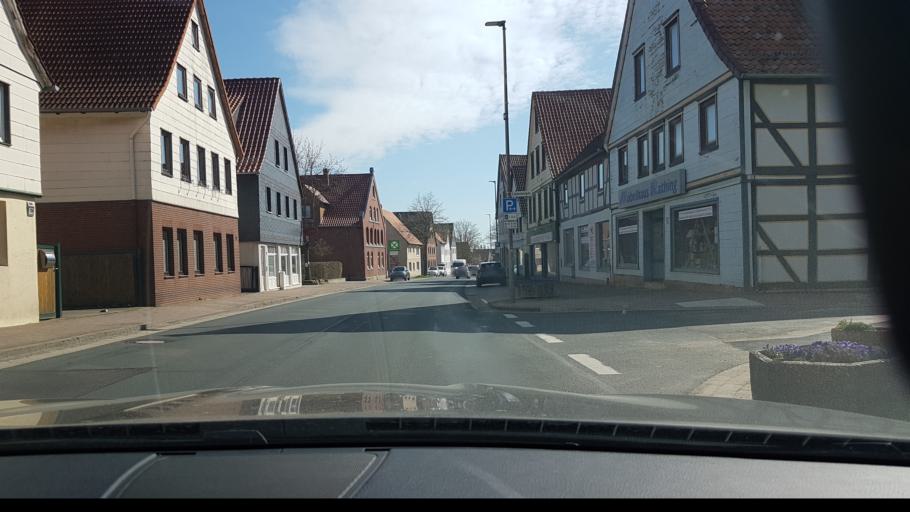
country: DE
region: Lower Saxony
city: Elze
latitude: 52.1833
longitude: 9.6723
